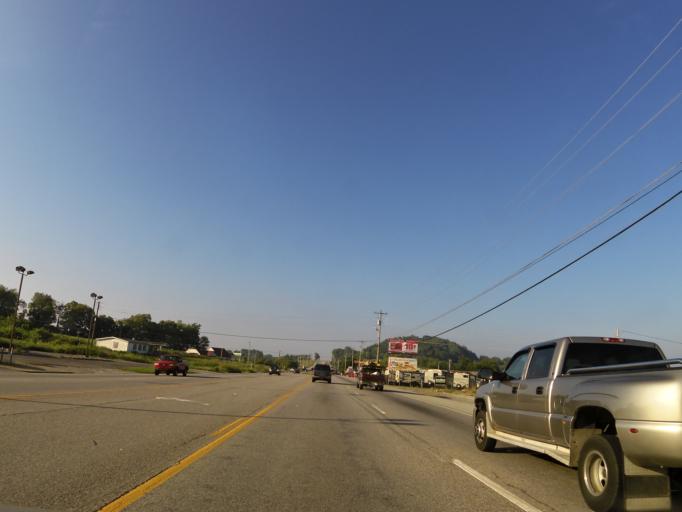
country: US
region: Tennessee
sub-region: Blount County
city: Alcoa
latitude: 35.8522
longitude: -83.9626
